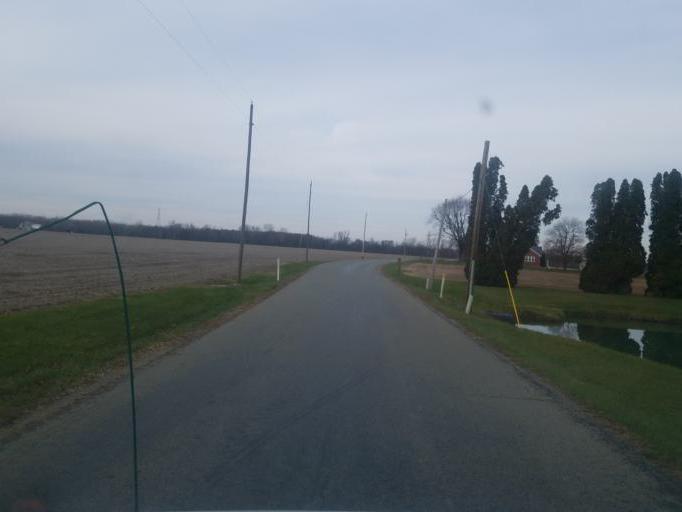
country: US
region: Ohio
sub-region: Knox County
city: Mount Vernon
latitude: 40.4034
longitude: -82.5124
